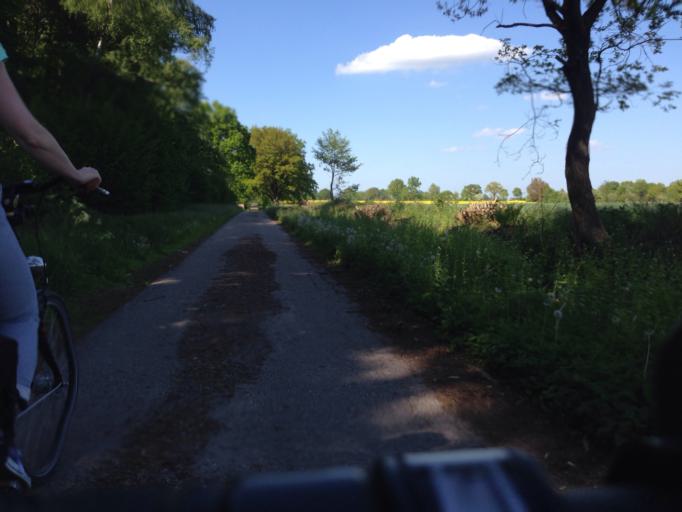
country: DE
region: Schleswig-Holstein
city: Braak
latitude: 53.6265
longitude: 10.2288
